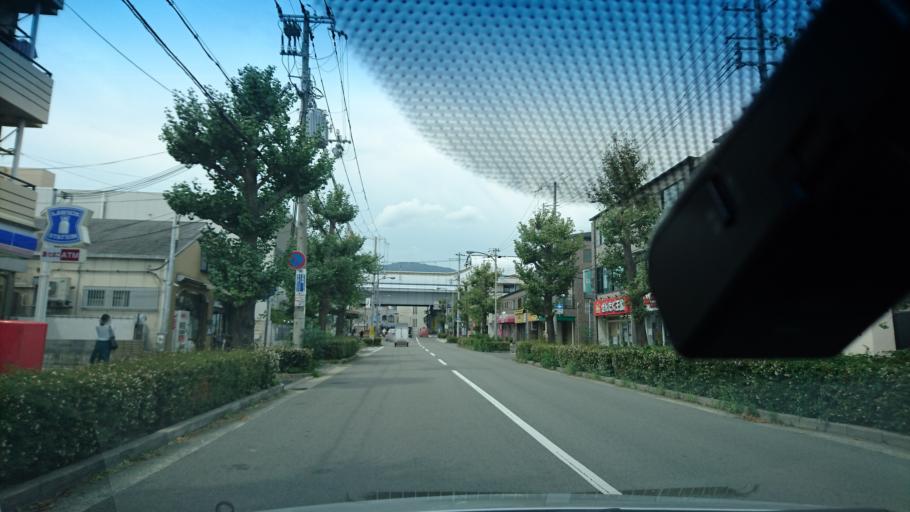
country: JP
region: Hyogo
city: Ashiya
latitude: 34.7298
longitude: 135.3175
